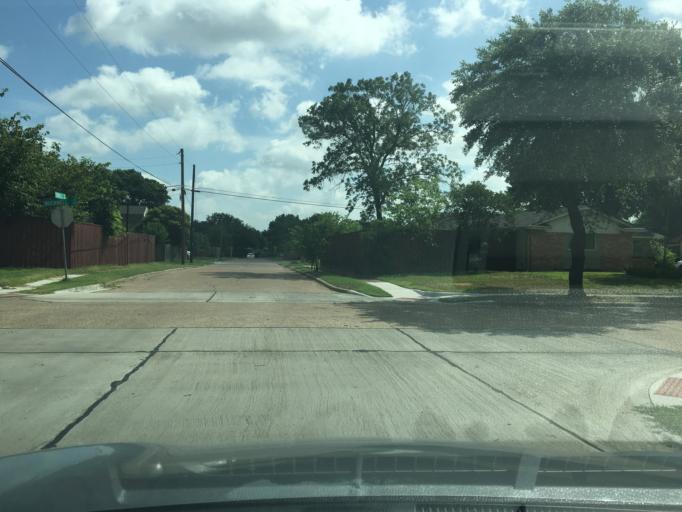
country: US
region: Texas
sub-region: Dallas County
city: Richardson
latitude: 32.9221
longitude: -96.6958
